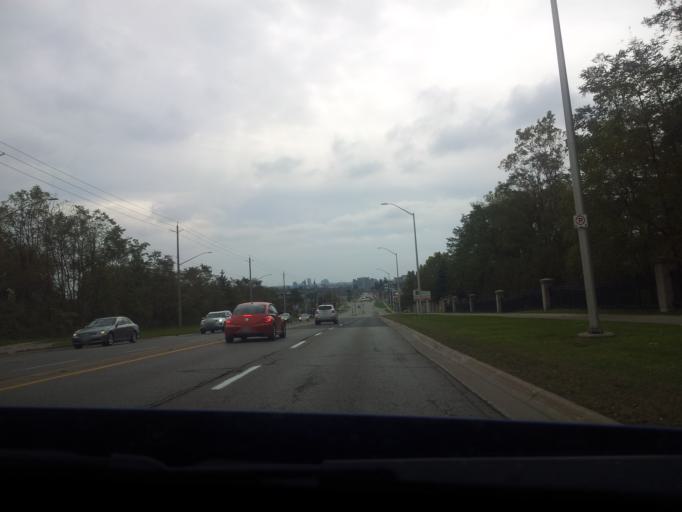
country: CA
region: Ontario
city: London
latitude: 43.0318
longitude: -81.2855
